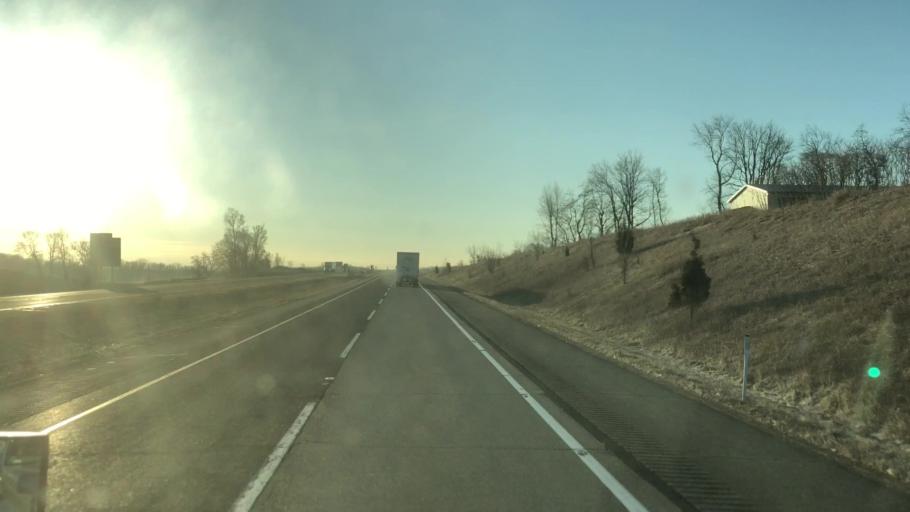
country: US
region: Indiana
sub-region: Steuben County
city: Fremont
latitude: 41.7168
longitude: -84.9556
